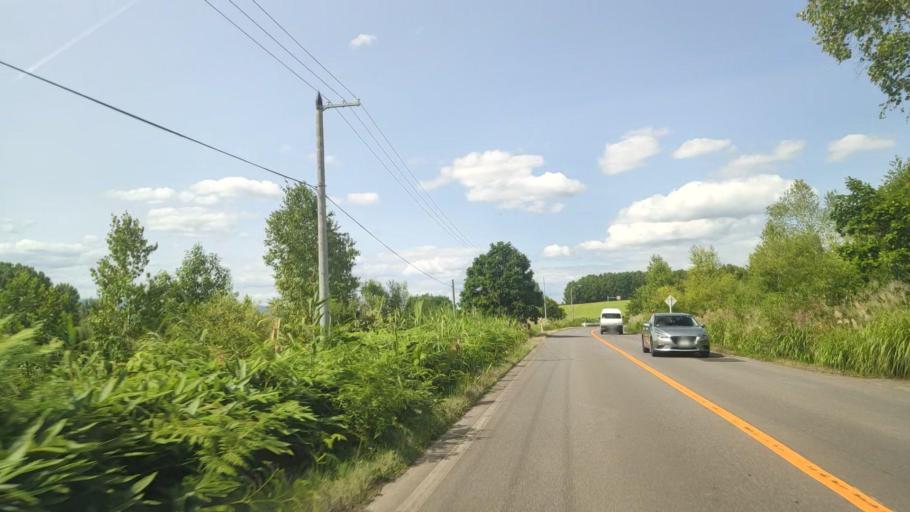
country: JP
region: Hokkaido
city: Nayoro
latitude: 44.2771
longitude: 142.4231
